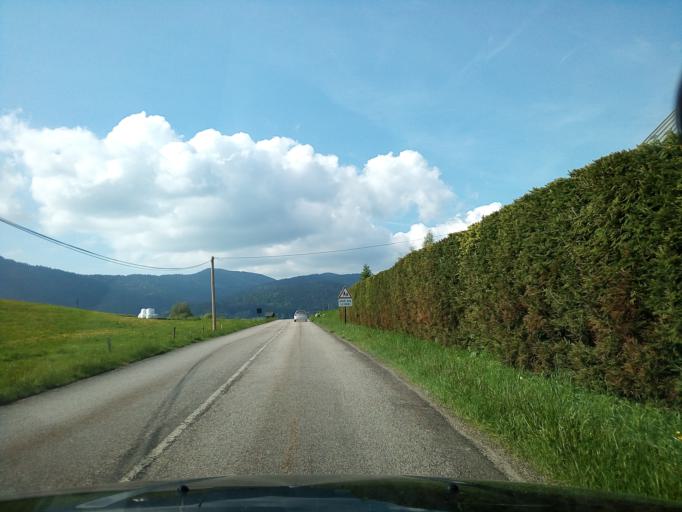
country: FR
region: Rhone-Alpes
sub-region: Departement de l'Isere
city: Autrans
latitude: 45.1679
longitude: 5.5528
